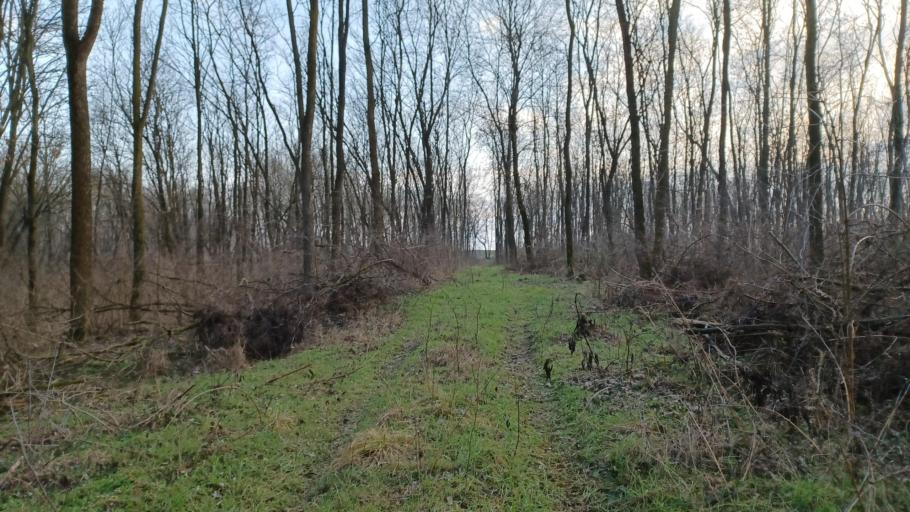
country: HU
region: Tolna
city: Tengelic
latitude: 46.5318
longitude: 18.7014
